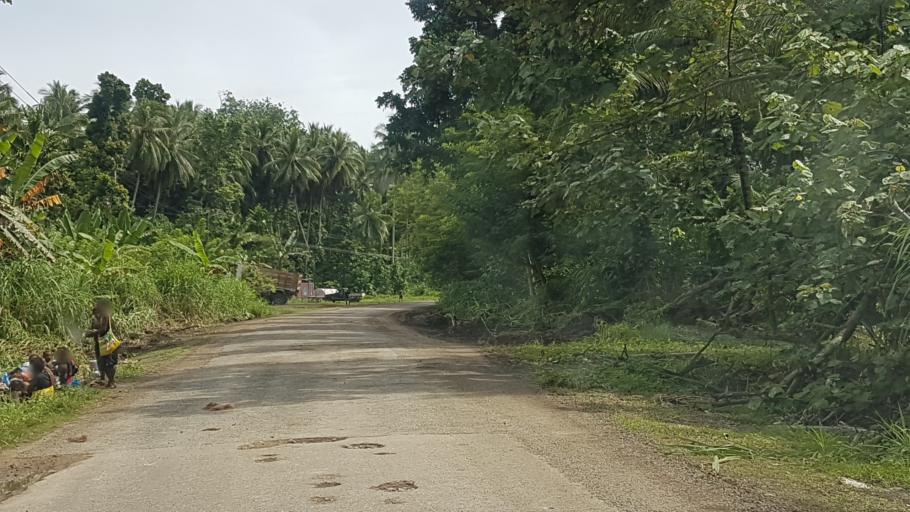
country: PG
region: Madang
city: Madang
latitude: -4.8786
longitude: 145.7939
